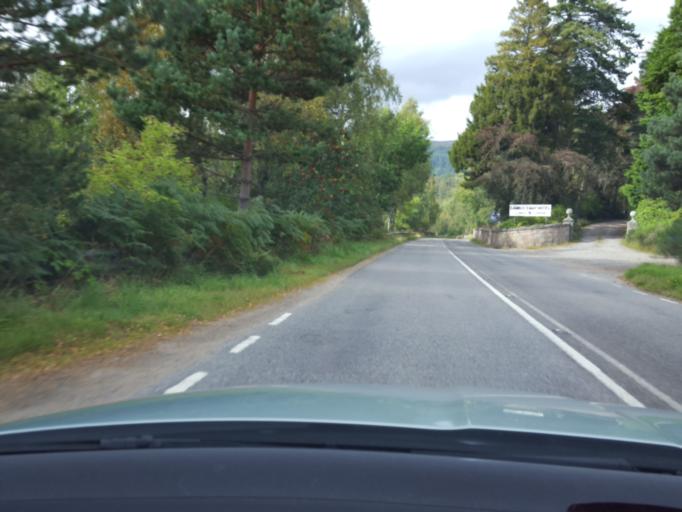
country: GB
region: Scotland
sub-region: Aberdeenshire
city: Ballater
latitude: 57.0653
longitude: -2.9552
